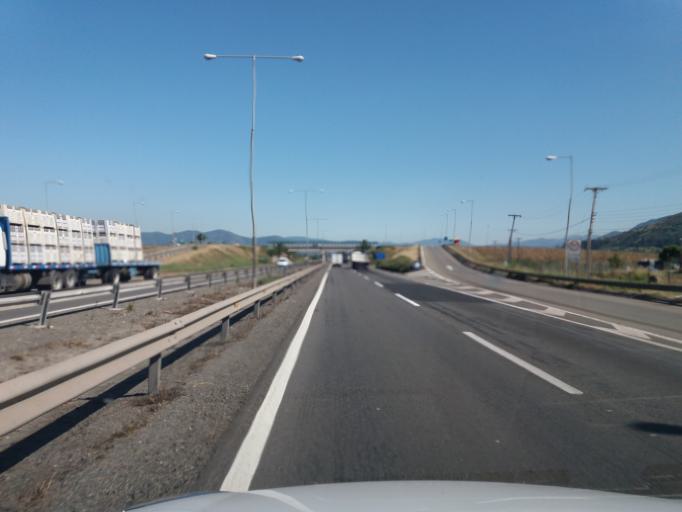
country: CL
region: Valparaiso
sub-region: Provincia de Quillota
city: Hacienda La Calera
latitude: -32.8077
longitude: -71.1500
